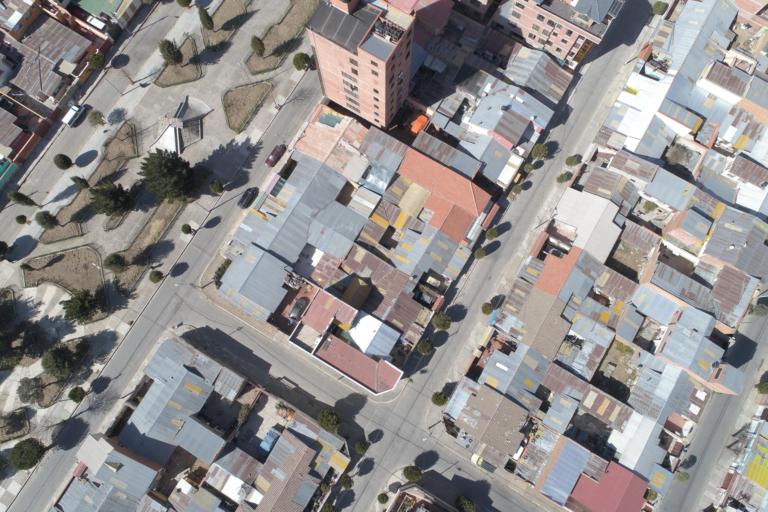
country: BO
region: La Paz
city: La Paz
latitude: -16.5287
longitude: -68.1554
